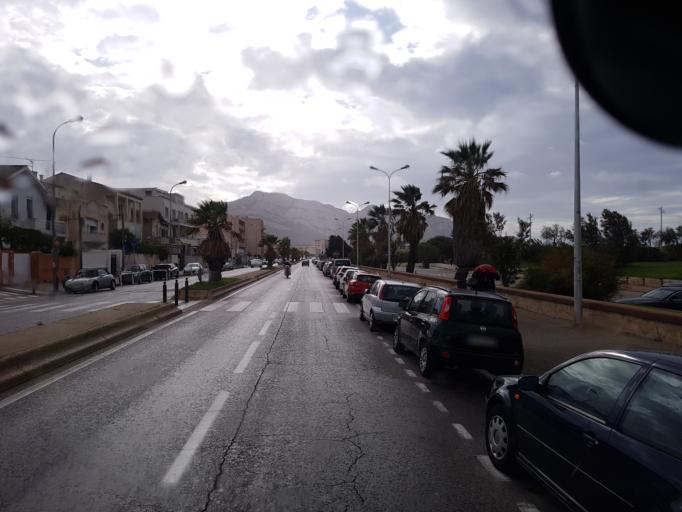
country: FR
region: Provence-Alpes-Cote d'Azur
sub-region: Departement des Bouches-du-Rhone
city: Marseille 08
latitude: 43.2527
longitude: 5.3758
